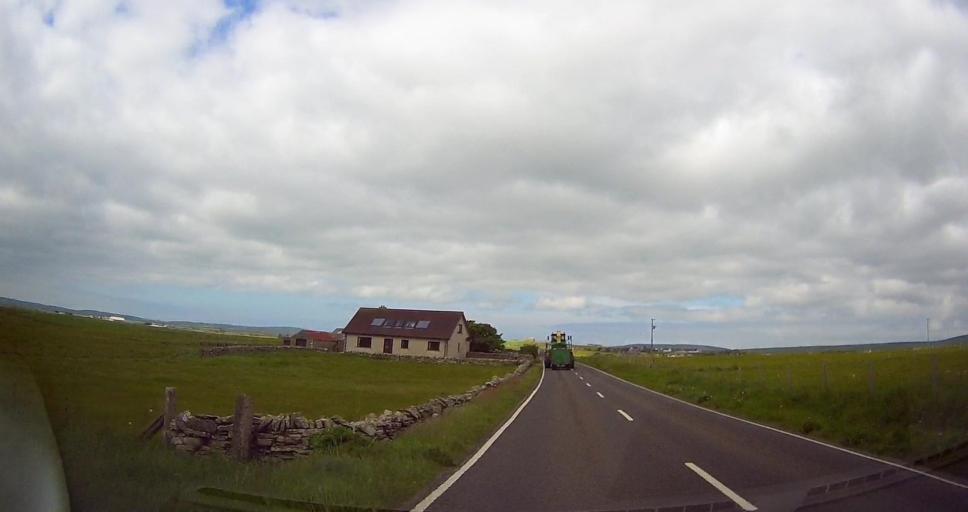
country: GB
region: Scotland
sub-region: Orkney Islands
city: Stromness
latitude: 59.0319
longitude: -3.1826
